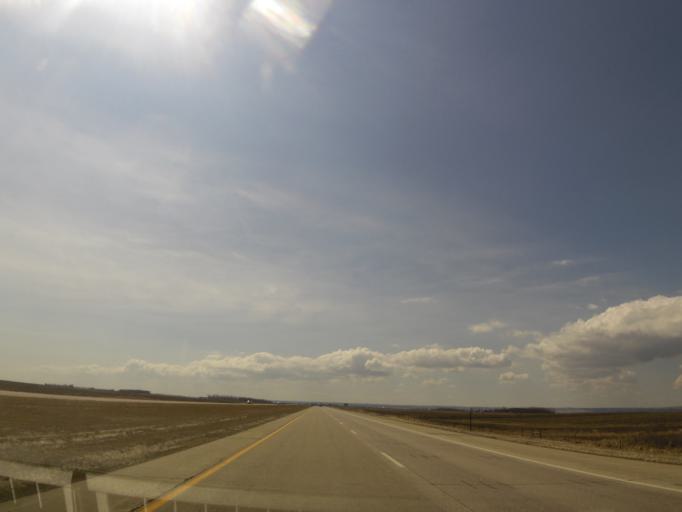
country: US
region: South Dakota
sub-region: Roberts County
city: Sisseton
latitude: 45.7231
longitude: -96.9478
